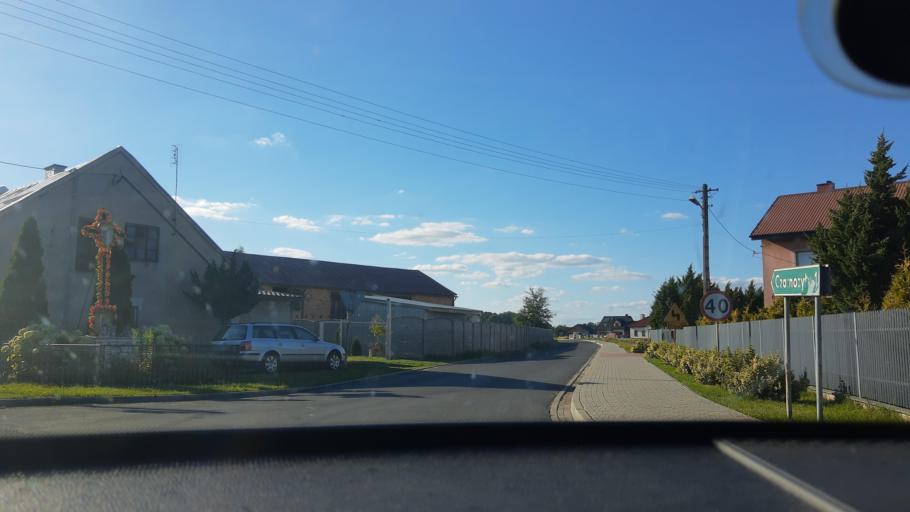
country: PL
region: Lodz Voivodeship
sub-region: Powiat wielunski
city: Czarnozyly
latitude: 51.2735
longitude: 18.5684
